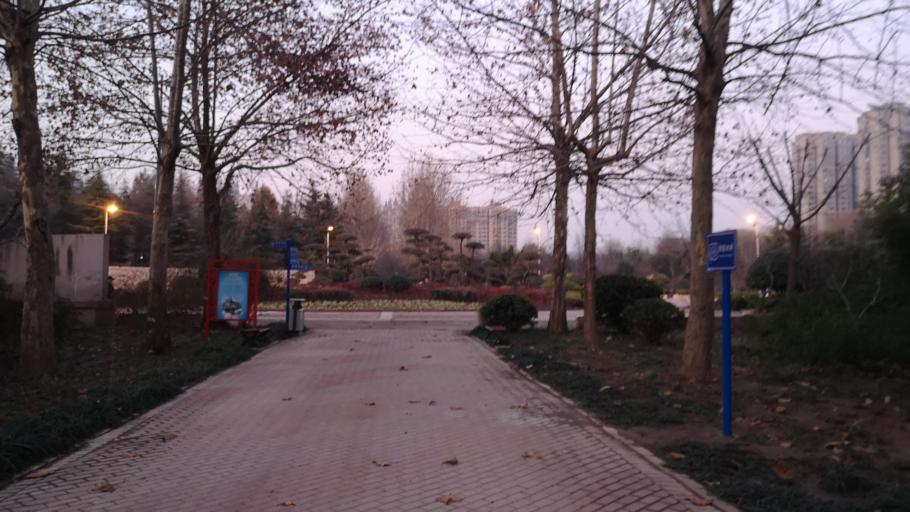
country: CN
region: Henan Sheng
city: Zhongyuanlu
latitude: 35.7430
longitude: 115.0631
